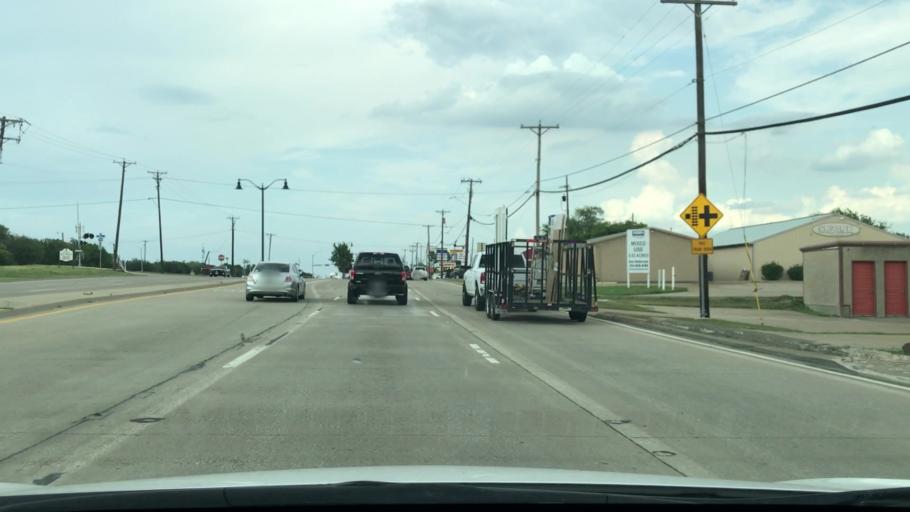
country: US
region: Texas
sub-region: Dallas County
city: Sachse
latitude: 32.9749
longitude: -96.5975
